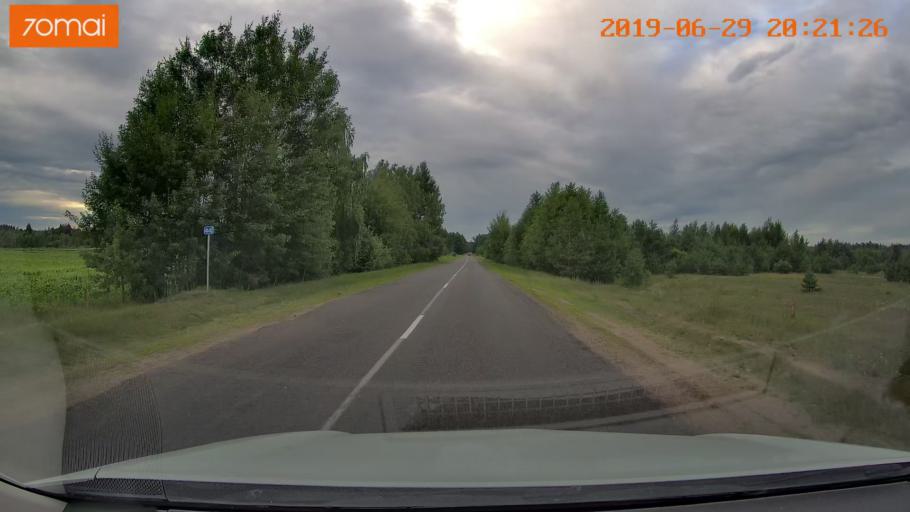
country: BY
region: Brest
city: Asnyezhytsy
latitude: 52.4198
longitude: 26.2530
